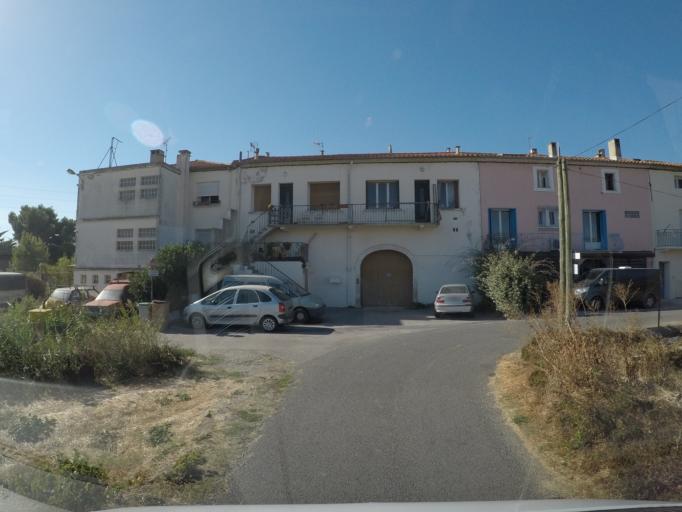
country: FR
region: Languedoc-Roussillon
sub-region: Departement de l'Aude
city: Narbonne
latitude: 43.1704
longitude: 3.0114
